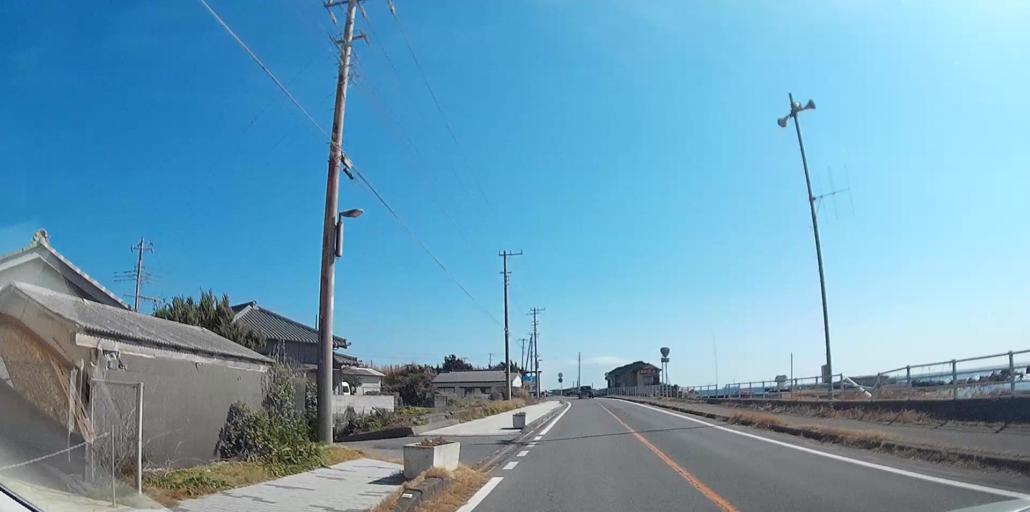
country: JP
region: Chiba
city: Tateyama
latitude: 34.9053
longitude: 139.8703
